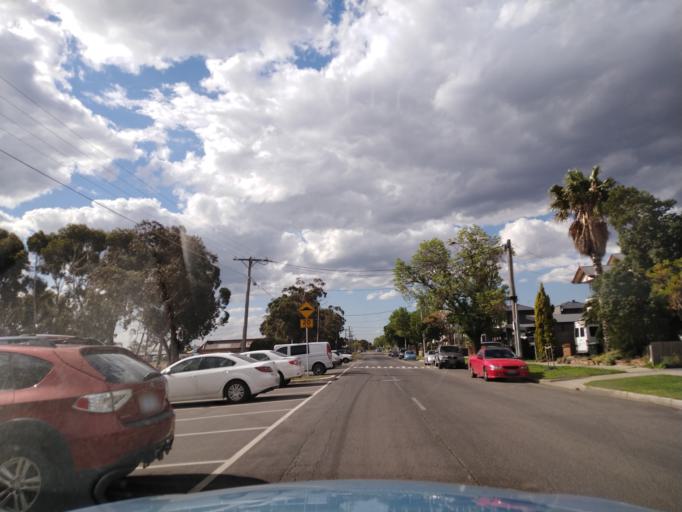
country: AU
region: Victoria
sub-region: Hobsons Bay
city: South Kingsville
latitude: -37.8463
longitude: 144.8634
